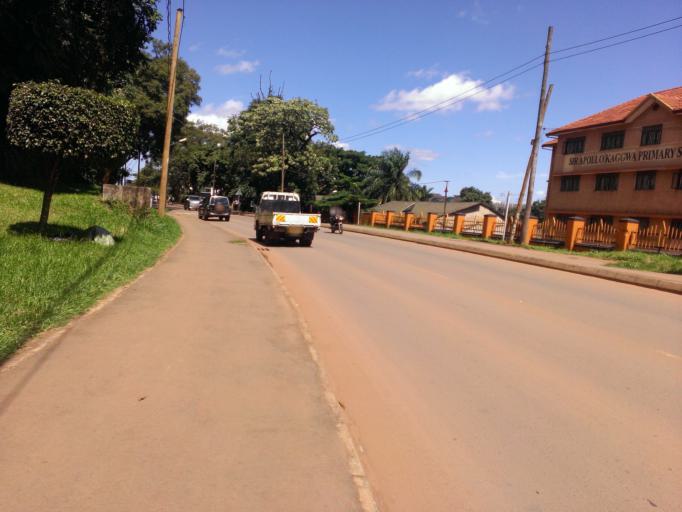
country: UG
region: Central Region
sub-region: Kampala District
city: Kampala
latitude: 0.3192
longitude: 32.5787
